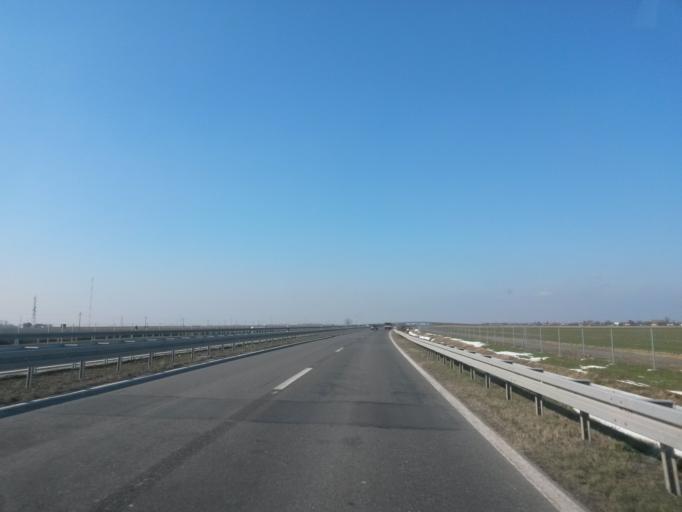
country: HR
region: Osjecko-Baranjska
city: Visnjevac
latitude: 45.5588
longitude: 18.6047
